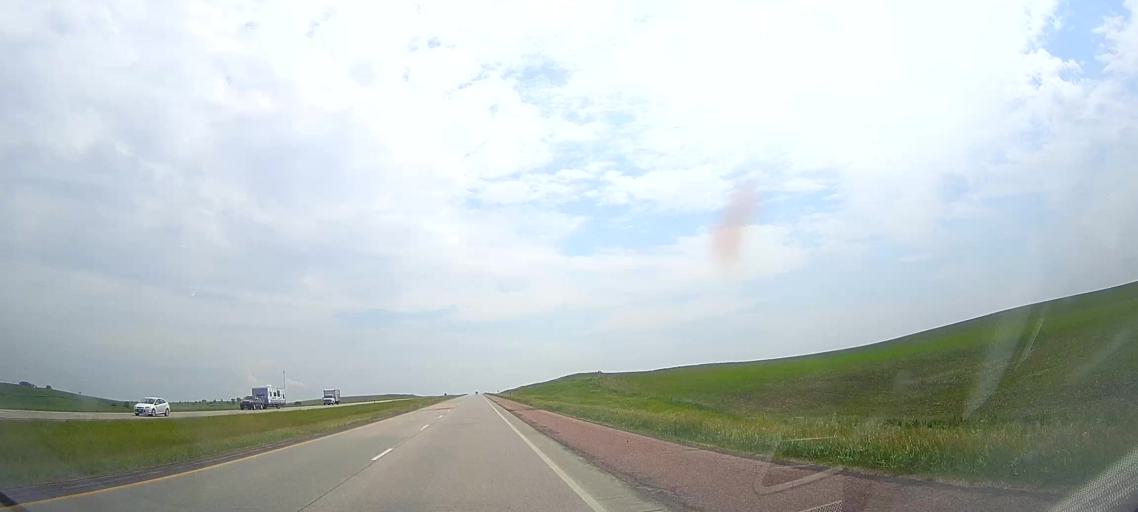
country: US
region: South Dakota
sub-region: Union County
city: Beresford
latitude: 42.9084
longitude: -96.7952
